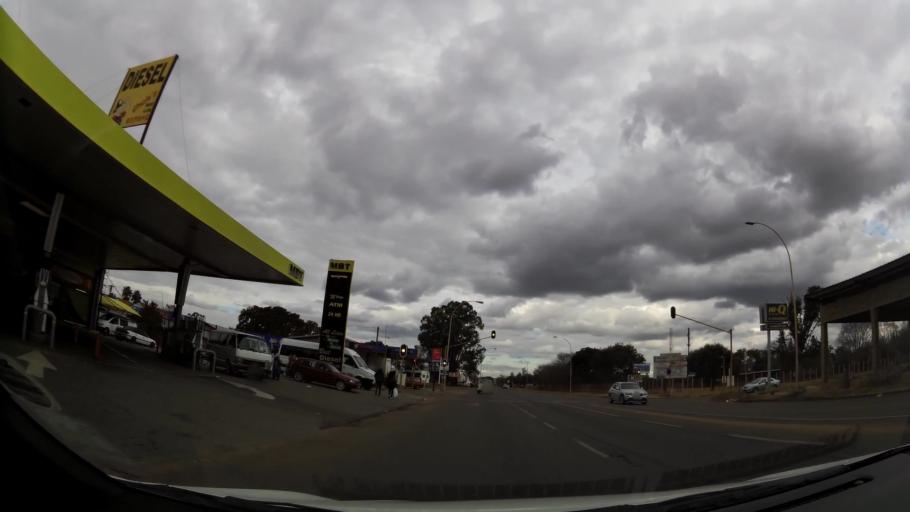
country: ZA
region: Limpopo
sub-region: Waterberg District Municipality
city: Modimolle
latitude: -24.7060
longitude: 28.4114
